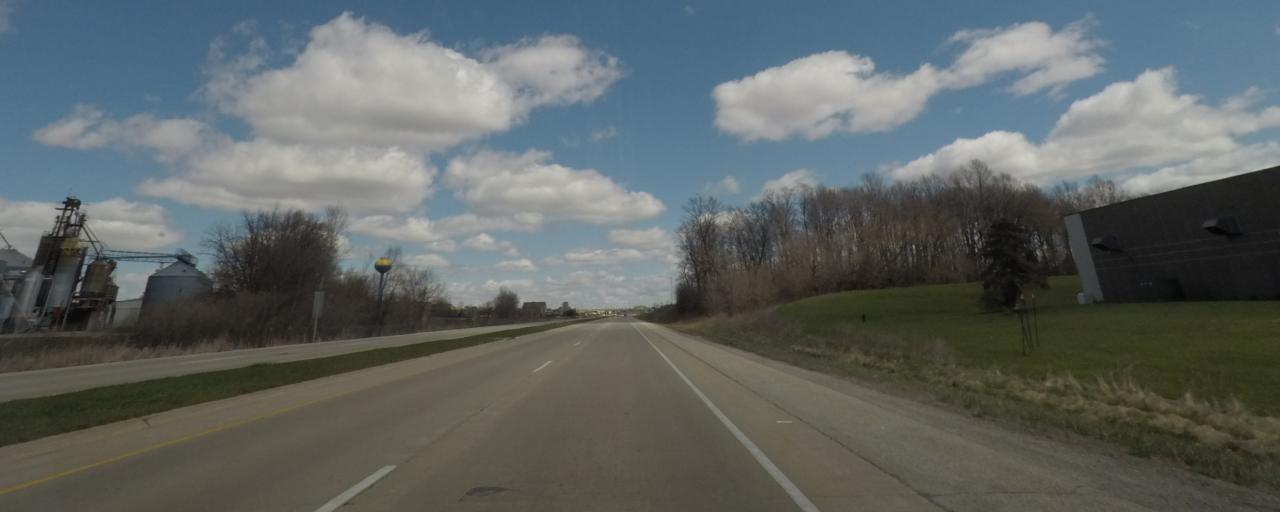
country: US
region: Wisconsin
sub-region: Jefferson County
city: Johnson Creek
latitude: 43.0767
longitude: -88.7667
